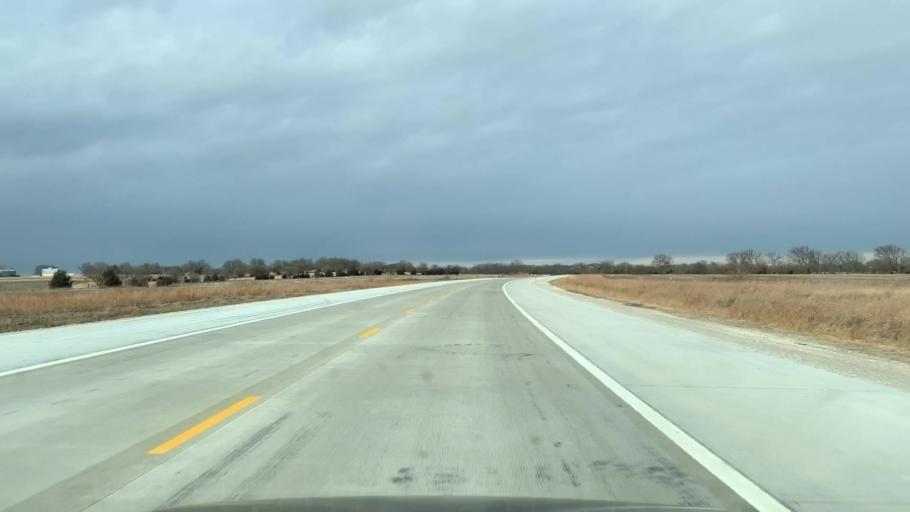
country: US
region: Kansas
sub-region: Allen County
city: Humboldt
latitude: 37.8550
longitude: -95.4087
